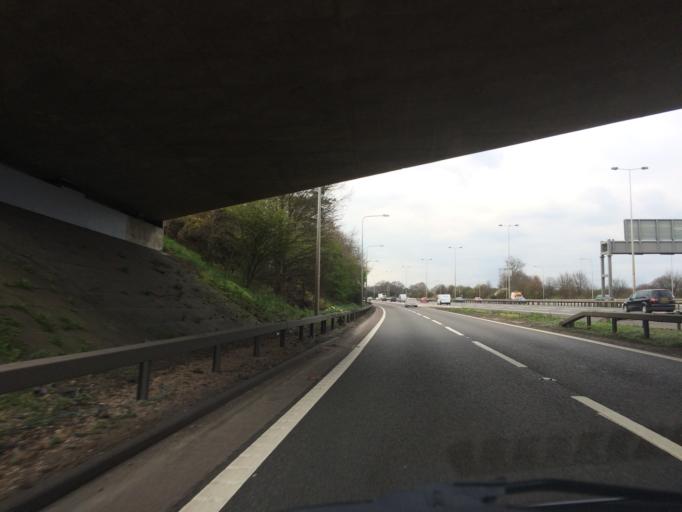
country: GB
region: England
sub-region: Surrey
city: Chertsey
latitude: 51.3773
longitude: -0.5110
